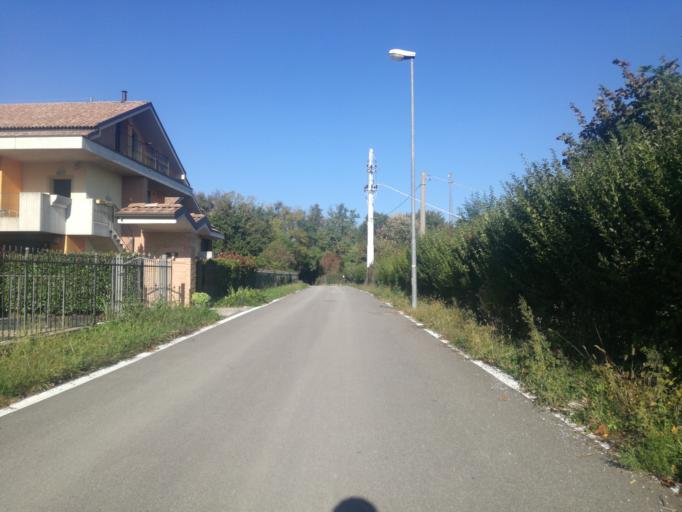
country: IT
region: Lombardy
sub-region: Provincia di Monza e Brianza
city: Porto d'Adda
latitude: 45.6509
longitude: 9.4830
